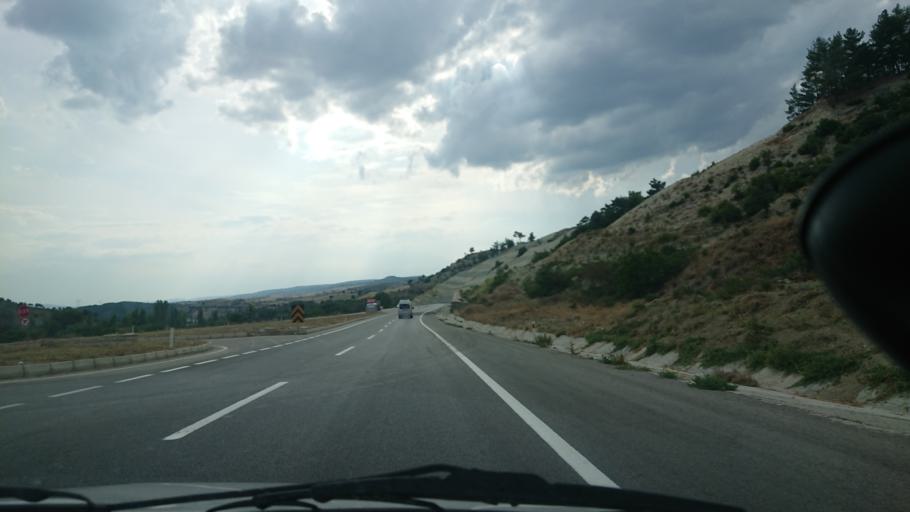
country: TR
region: Kuetahya
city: Gediz
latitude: 39.0444
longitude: 29.4304
